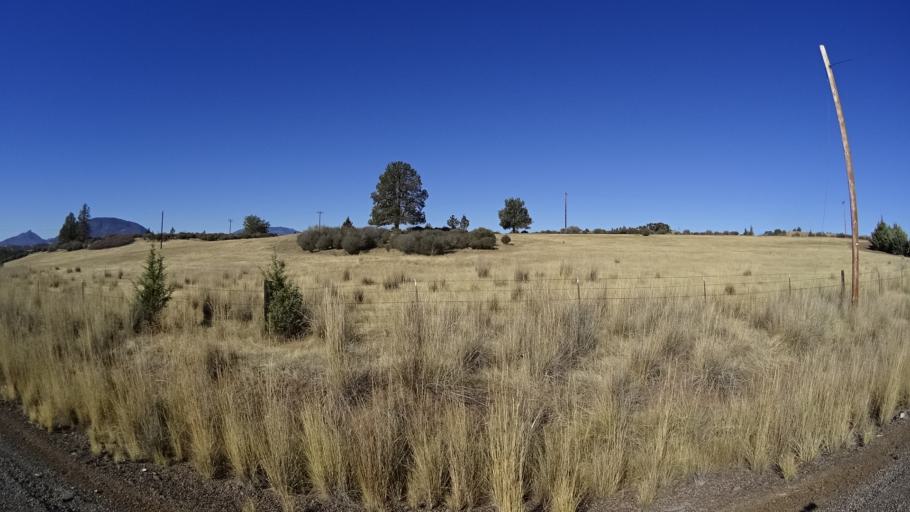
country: US
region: California
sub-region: Siskiyou County
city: Montague
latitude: 41.8991
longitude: -122.3918
